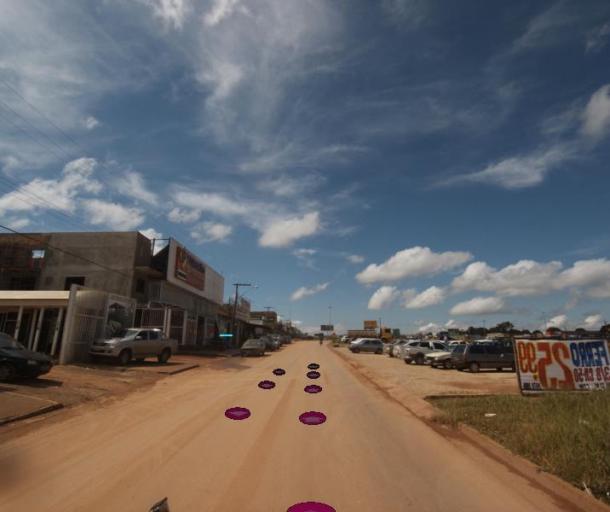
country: BR
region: Federal District
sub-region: Brasilia
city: Brasilia
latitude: -15.7448
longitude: -48.2662
